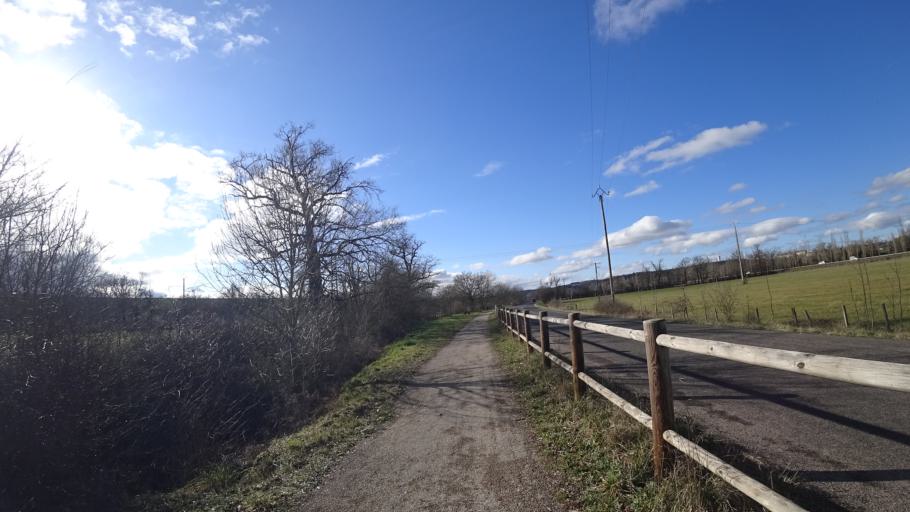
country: FR
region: Midi-Pyrenees
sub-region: Departement de l'Aveyron
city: Sebazac-Concoures
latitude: 44.3733
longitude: 2.6039
